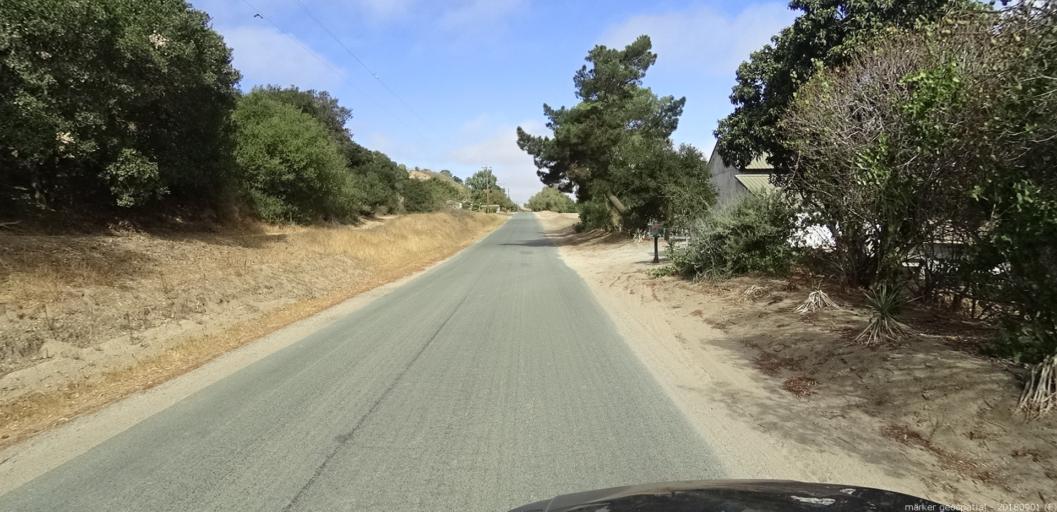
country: US
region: California
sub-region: Monterey County
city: Soledad
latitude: 36.3862
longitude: -121.3599
